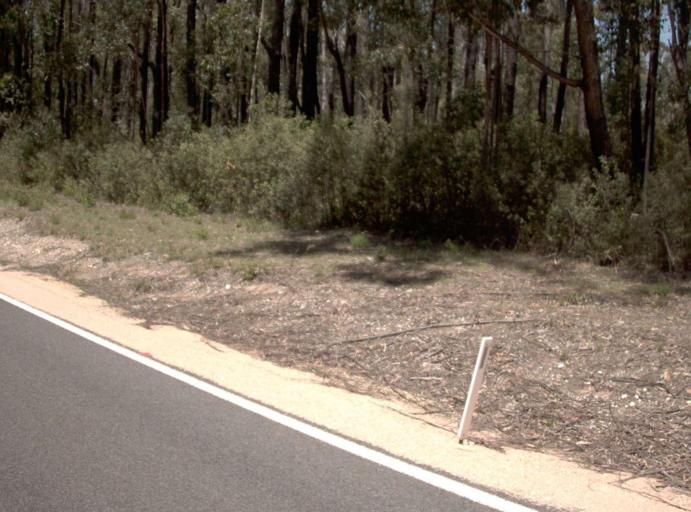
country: AU
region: Victoria
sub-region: East Gippsland
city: Lakes Entrance
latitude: -37.6857
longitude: 148.7621
